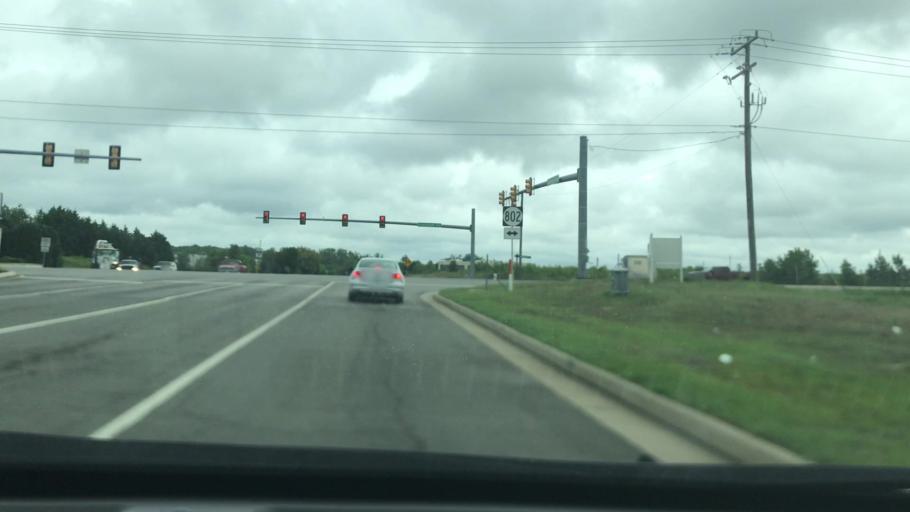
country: US
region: Virginia
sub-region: Hanover County
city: Ashland
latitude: 37.7189
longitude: -77.4526
